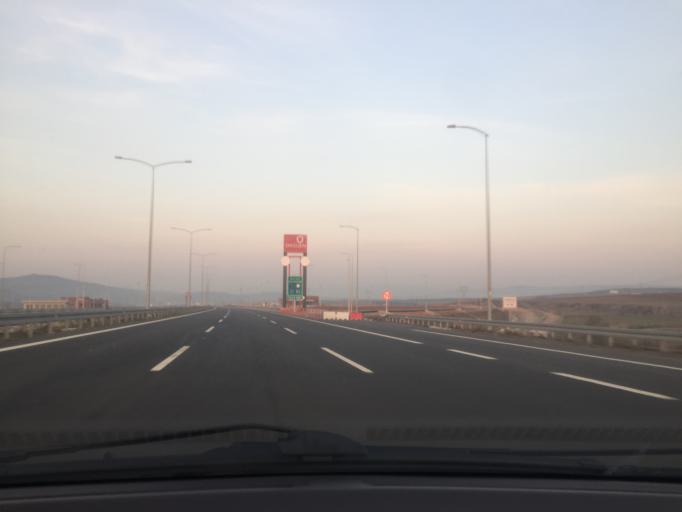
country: TR
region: Bursa
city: Mahmudiye
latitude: 40.2723
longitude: 28.6063
